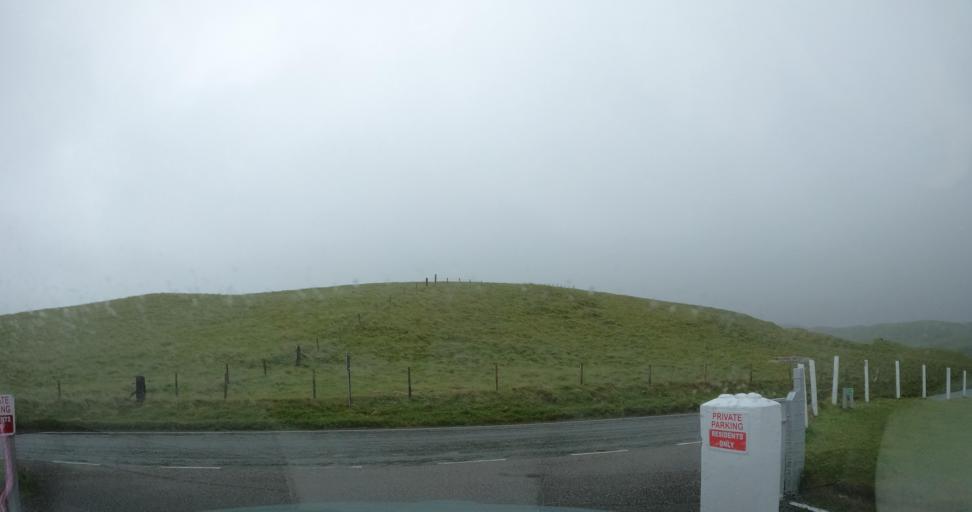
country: GB
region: Scotland
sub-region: Eilean Siar
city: Barra
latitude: 56.9759
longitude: -7.5178
